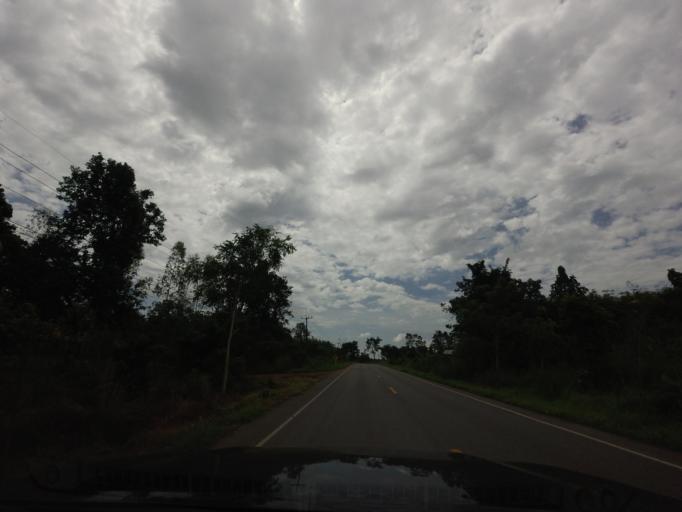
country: TH
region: Changwat Udon Thani
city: Nam Som
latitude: 17.8187
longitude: 102.2723
